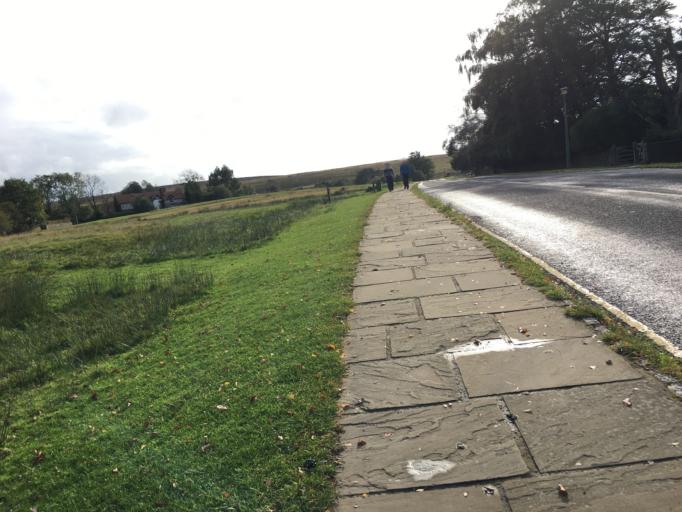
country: GB
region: England
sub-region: North Yorkshire
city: Sleights
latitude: 54.3969
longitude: -0.7238
